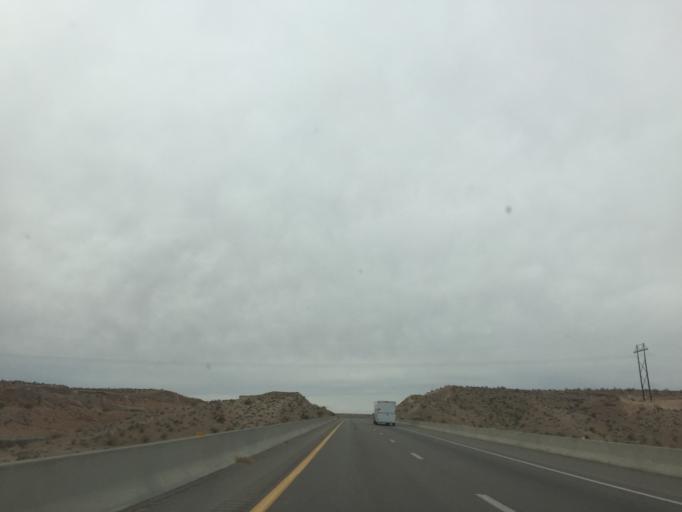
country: US
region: Nevada
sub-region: Clark County
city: Bunkerville
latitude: 36.7668
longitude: -114.2007
